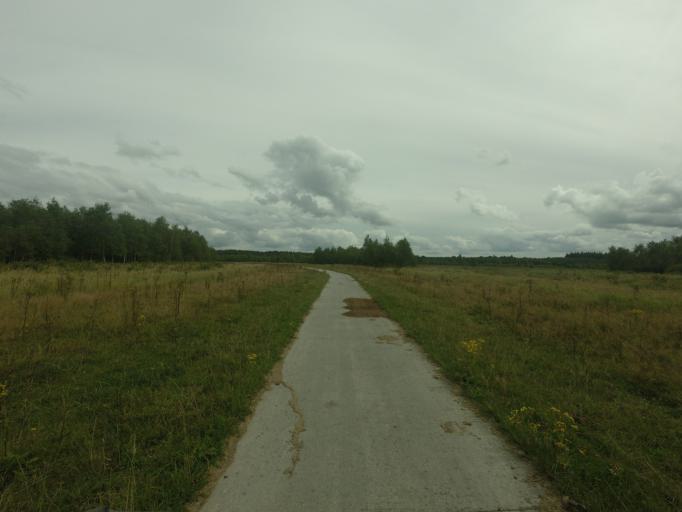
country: NL
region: Drenthe
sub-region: Gemeente Westerveld
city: Dwingeloo
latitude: 52.9841
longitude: 6.3826
